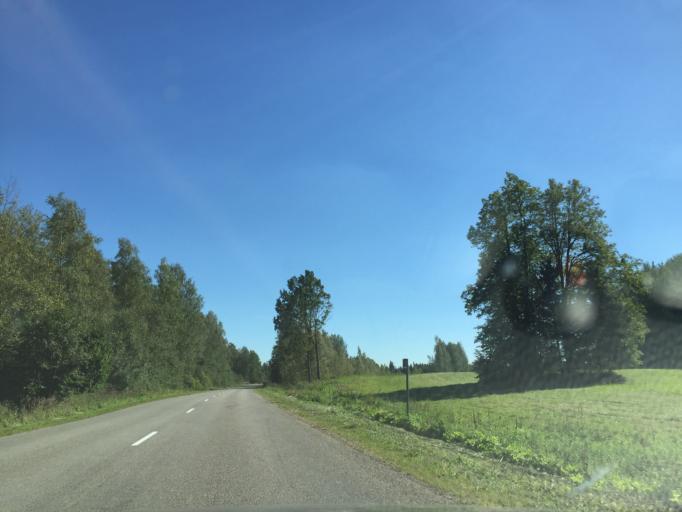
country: LV
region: Akniste
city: Akniste
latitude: 56.0740
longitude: 25.8866
